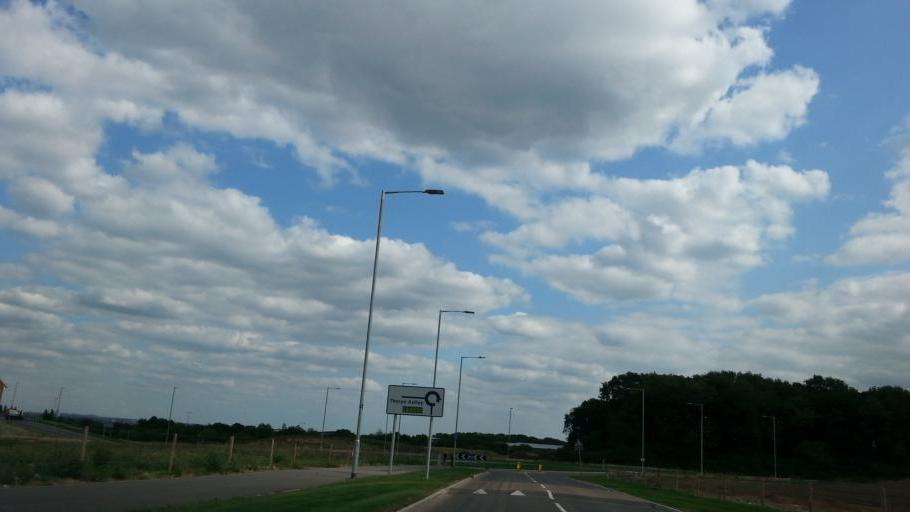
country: GB
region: England
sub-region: Leicestershire
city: Enderby
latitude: 52.6126
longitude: -1.2056
